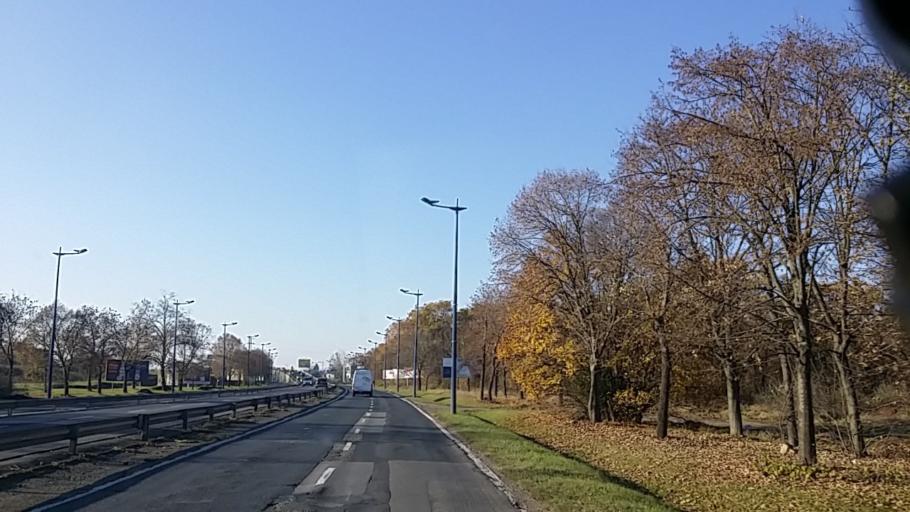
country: HU
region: Budapest
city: Budapest XVIII. keruelet
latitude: 47.4508
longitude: 19.2022
